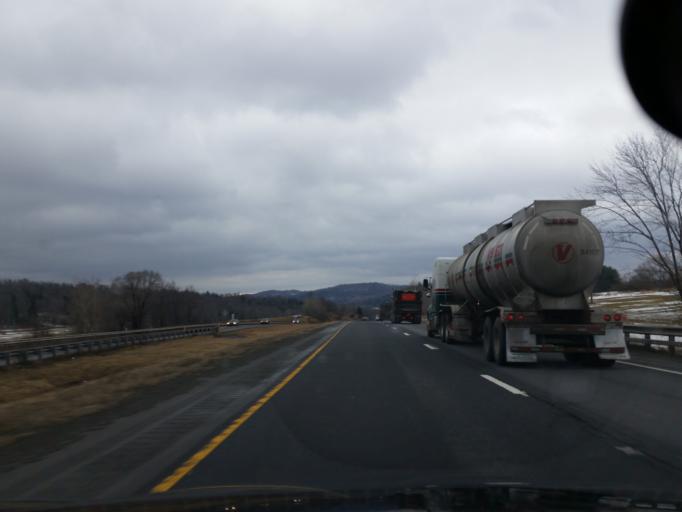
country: US
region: Pennsylvania
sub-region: Lackawanna County
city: Dalton
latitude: 41.6707
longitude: -75.6798
